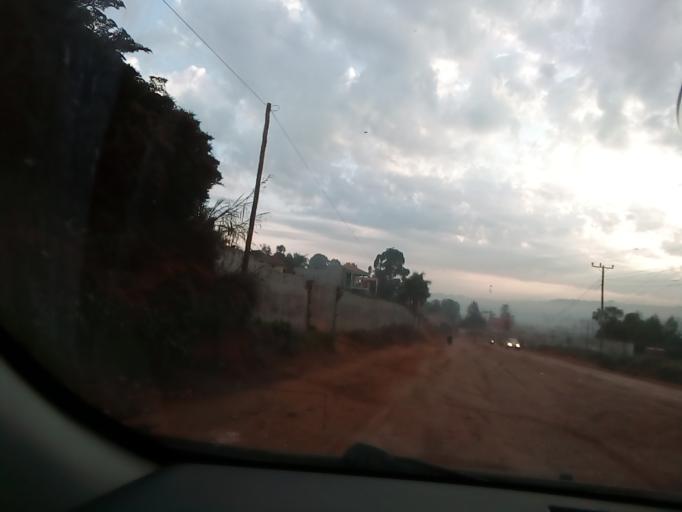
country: UG
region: Central Region
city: Masaka
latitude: -0.3313
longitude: 31.7455
